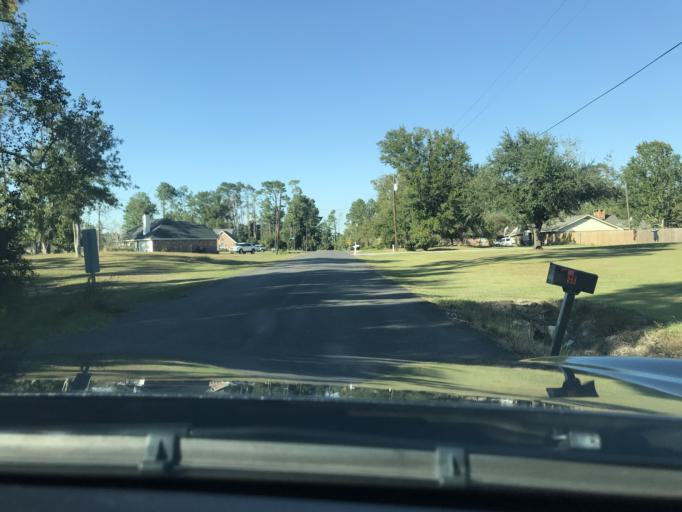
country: US
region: Louisiana
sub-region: Calcasieu Parish
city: Westlake
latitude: 30.3159
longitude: -93.2717
